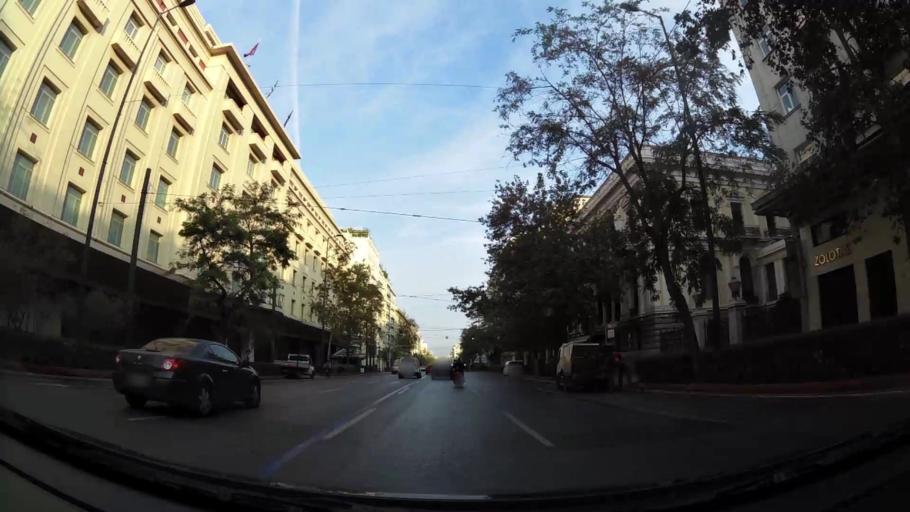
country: GR
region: Attica
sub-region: Nomarchia Athinas
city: Athens
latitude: 37.9774
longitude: 23.7353
